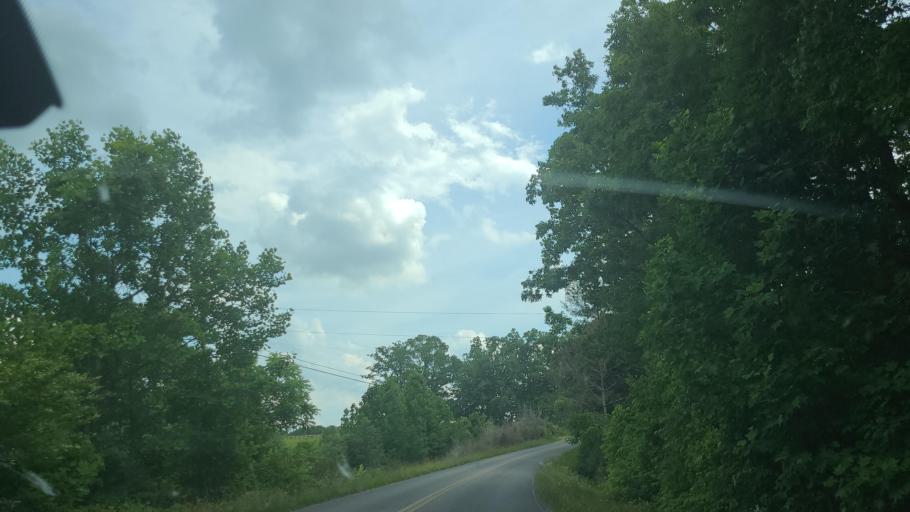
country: US
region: Tennessee
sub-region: Cumberland County
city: Lake Tansi
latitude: 35.7921
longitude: -85.0494
